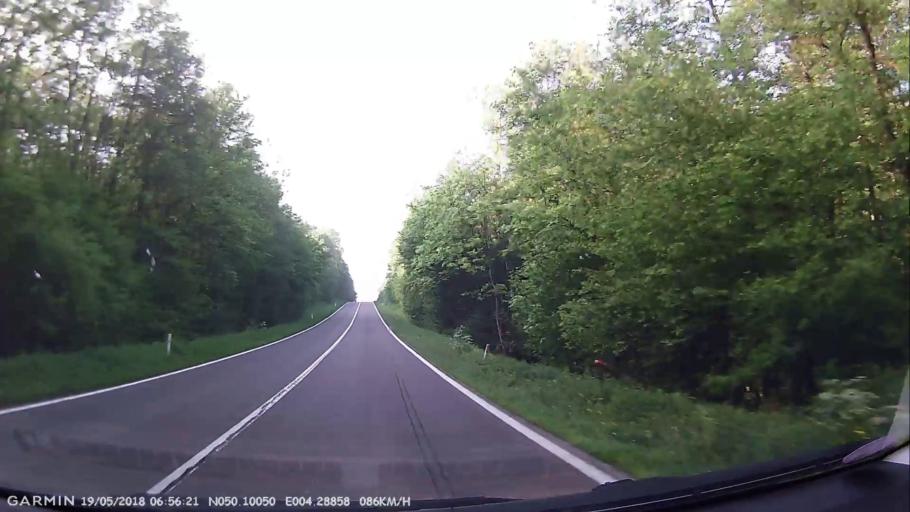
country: BE
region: Wallonia
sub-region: Province du Hainaut
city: Chimay
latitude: 50.1002
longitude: 4.2887
